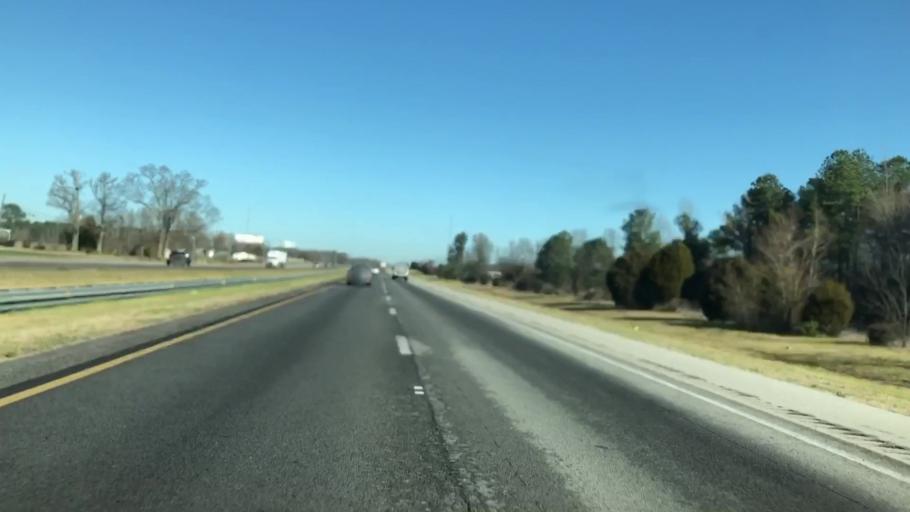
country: US
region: Alabama
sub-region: Limestone County
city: Athens
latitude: 34.8730
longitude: -86.9220
